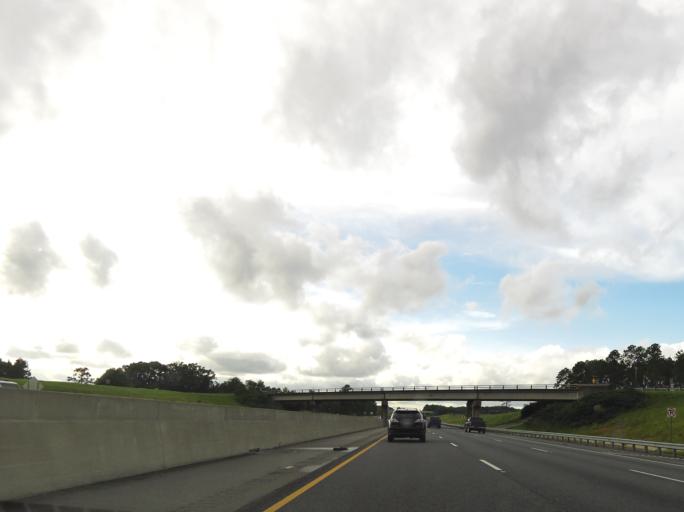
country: US
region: Georgia
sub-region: Turner County
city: Ashburn
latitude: 31.6648
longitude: -83.6070
